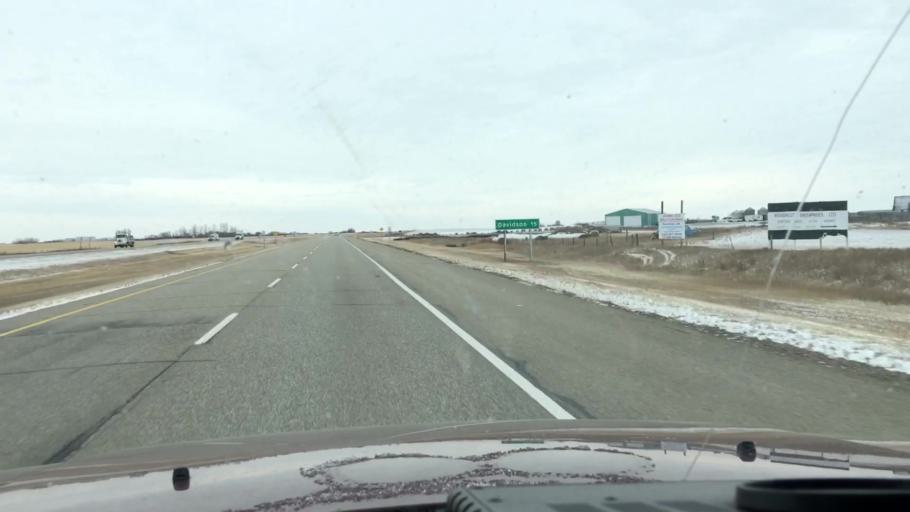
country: CA
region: Saskatchewan
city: Watrous
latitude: 51.3675
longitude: -106.1334
